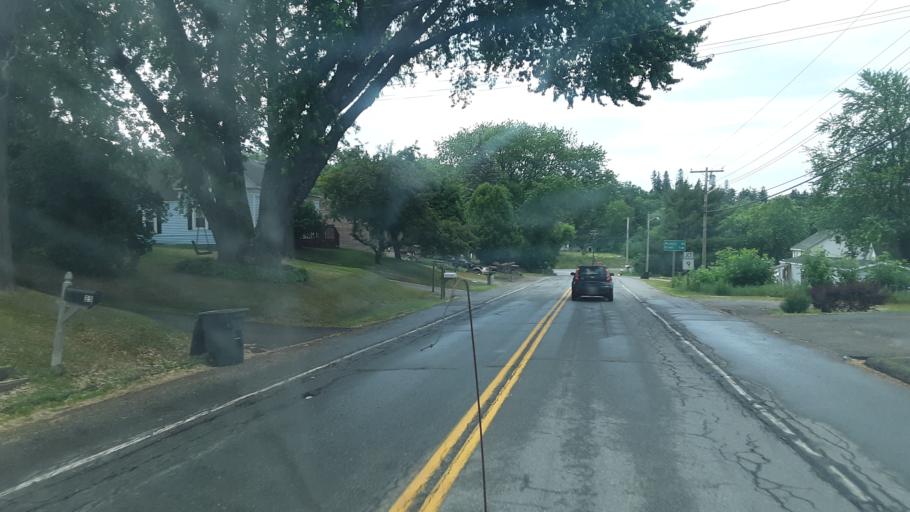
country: US
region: Maine
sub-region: Penobscot County
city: Eddington
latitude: 44.8258
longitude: -68.6935
